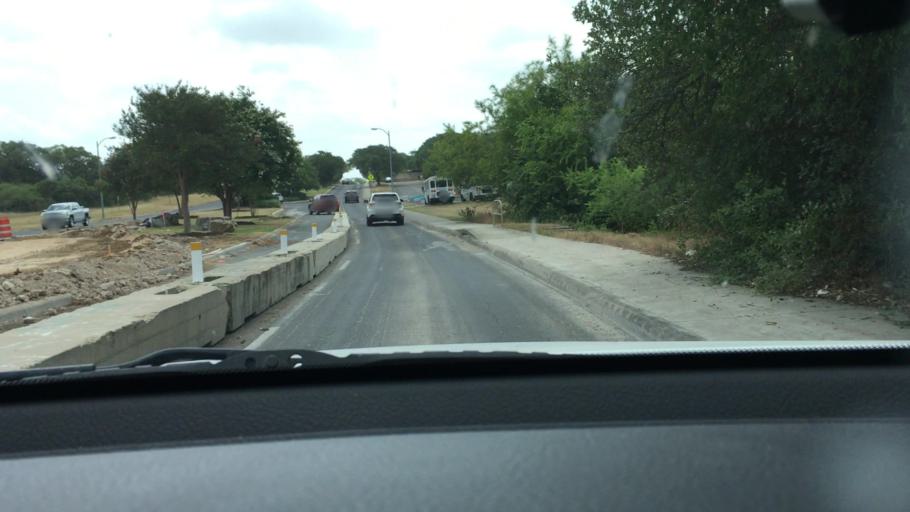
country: US
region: Texas
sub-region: Bexar County
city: Hollywood Park
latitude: 29.6301
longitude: -98.4581
